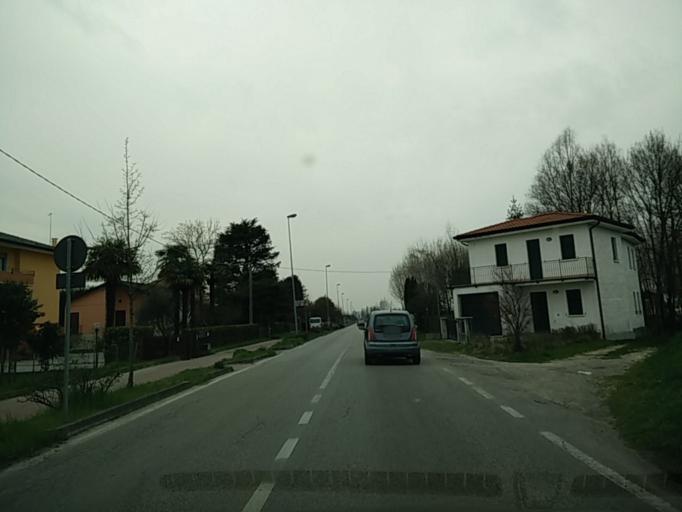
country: IT
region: Veneto
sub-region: Provincia di Venezia
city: Noale
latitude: 45.5517
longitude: 12.0615
